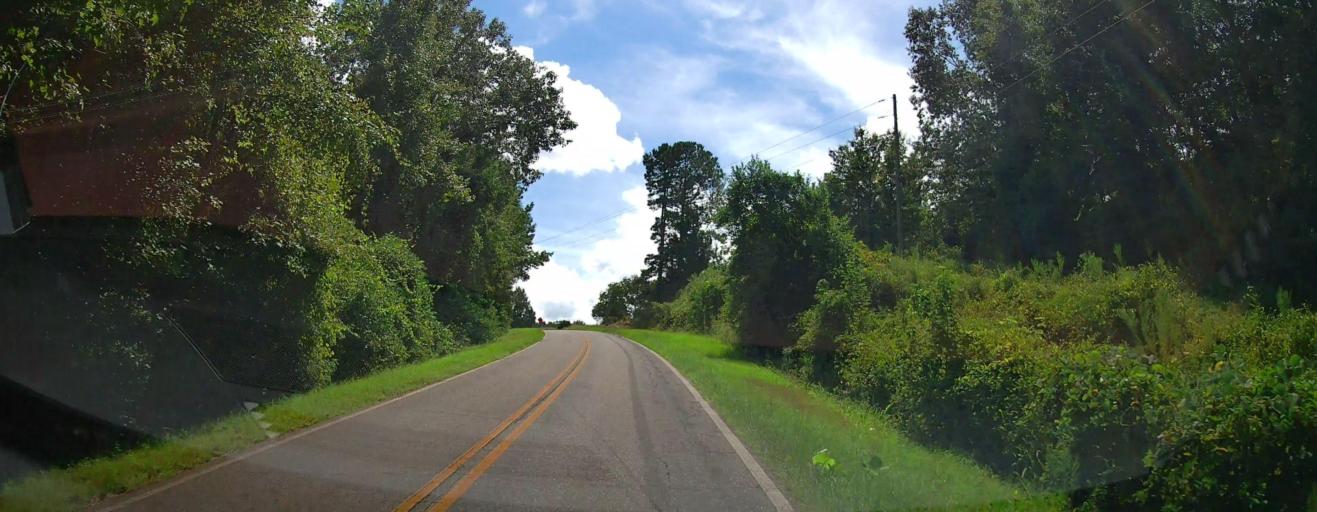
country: US
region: Georgia
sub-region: Macon County
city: Marshallville
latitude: 32.4759
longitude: -83.8666
